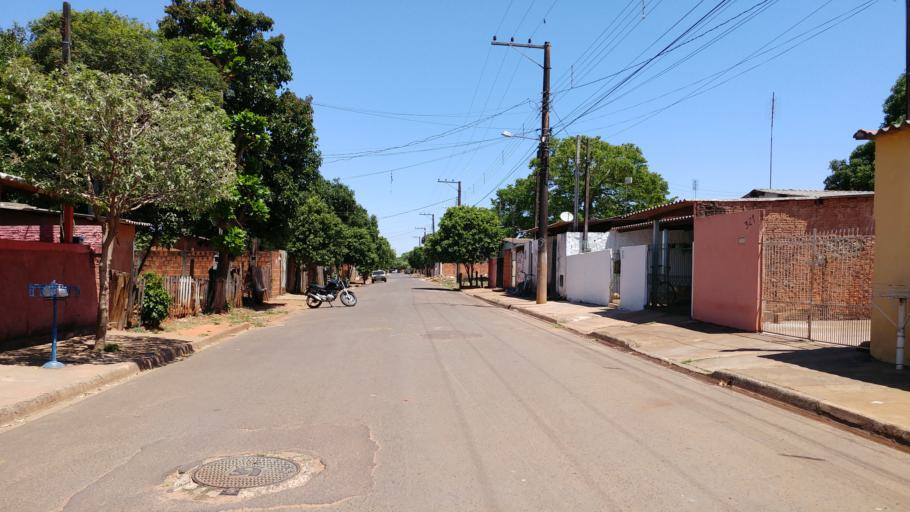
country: BR
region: Sao Paulo
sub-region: Paraguacu Paulista
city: Paraguacu Paulista
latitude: -22.4071
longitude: -50.5685
